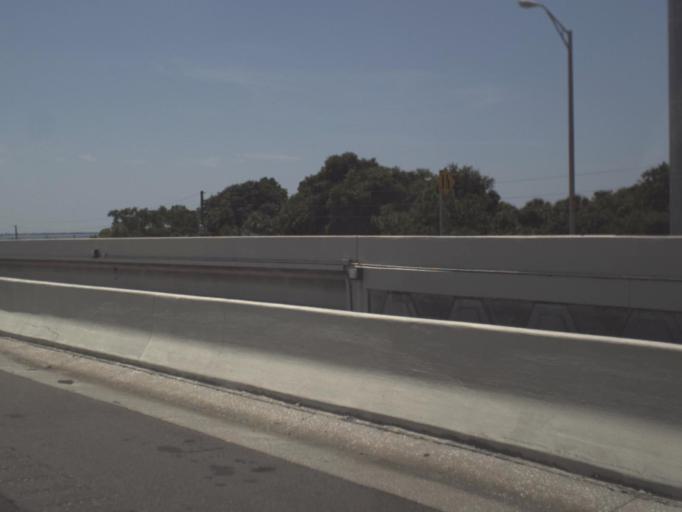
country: US
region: Florida
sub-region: Pinellas County
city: Gulfport
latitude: 27.7093
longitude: -82.6793
